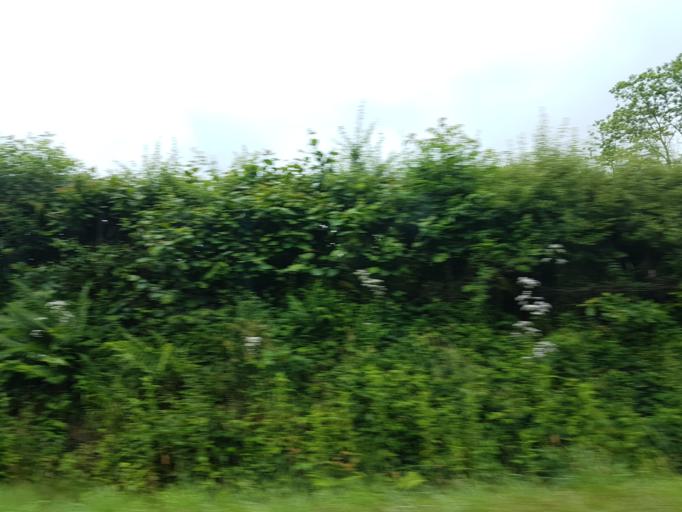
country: FR
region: Bourgogne
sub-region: Departement de la Nievre
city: Lormes
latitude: 47.1630
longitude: 3.8412
